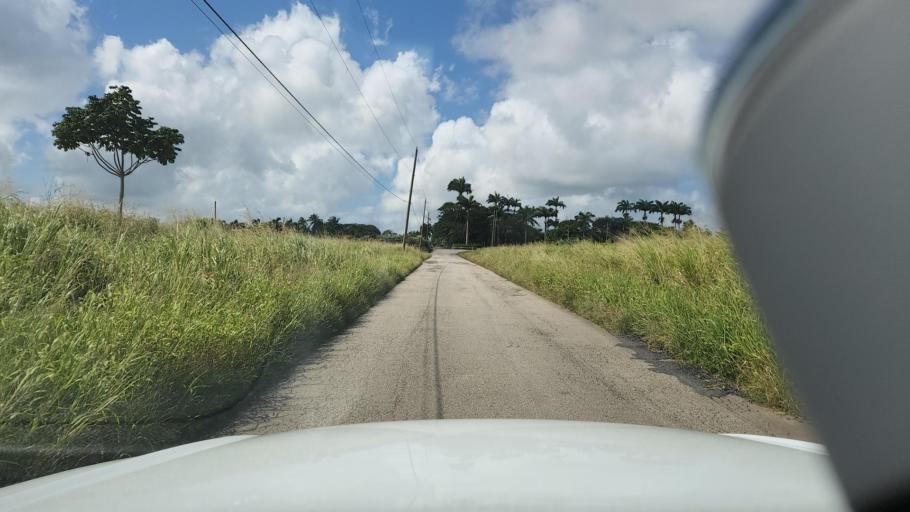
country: BB
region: Saint John
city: Four Cross Roads
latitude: 13.1890
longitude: -59.5045
